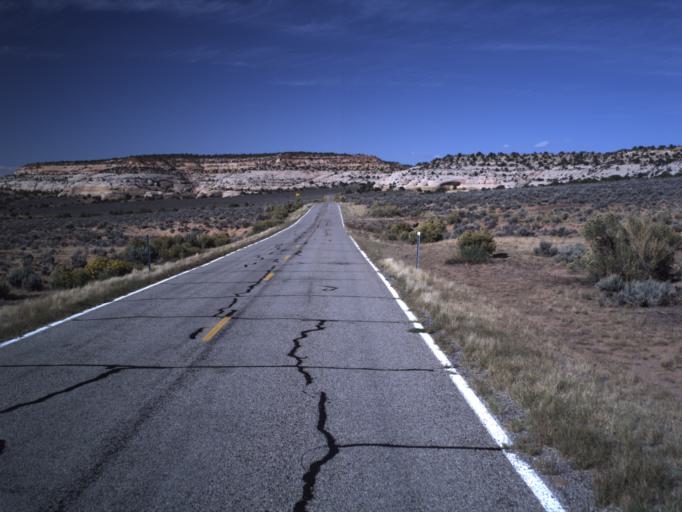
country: US
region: Utah
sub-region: San Juan County
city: Monticello
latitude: 38.0471
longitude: -109.4121
